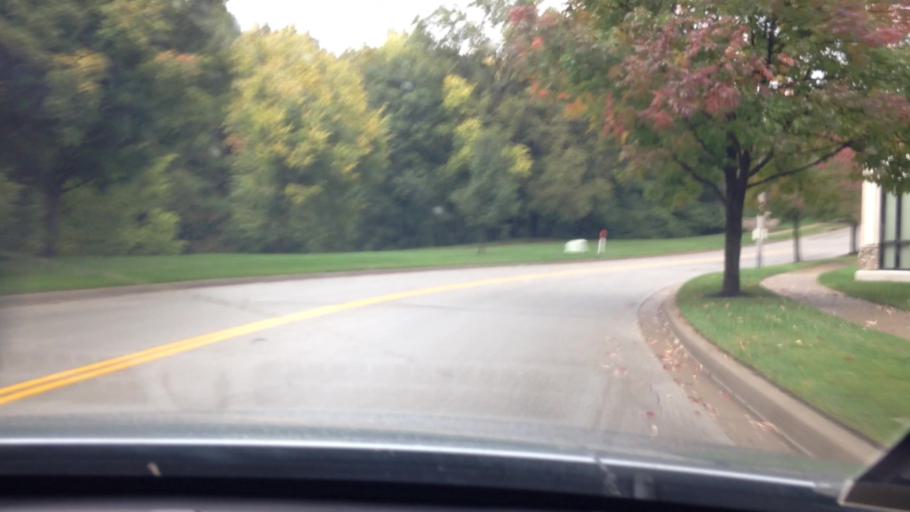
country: US
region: Missouri
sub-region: Platte County
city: Riverside
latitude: 39.1698
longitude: -94.5993
